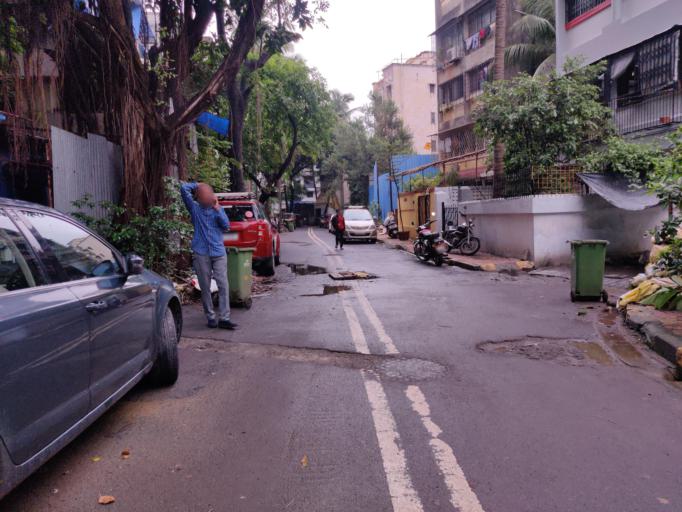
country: IN
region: Maharashtra
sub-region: Mumbai Suburban
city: Borivli
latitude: 19.2533
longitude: 72.8576
